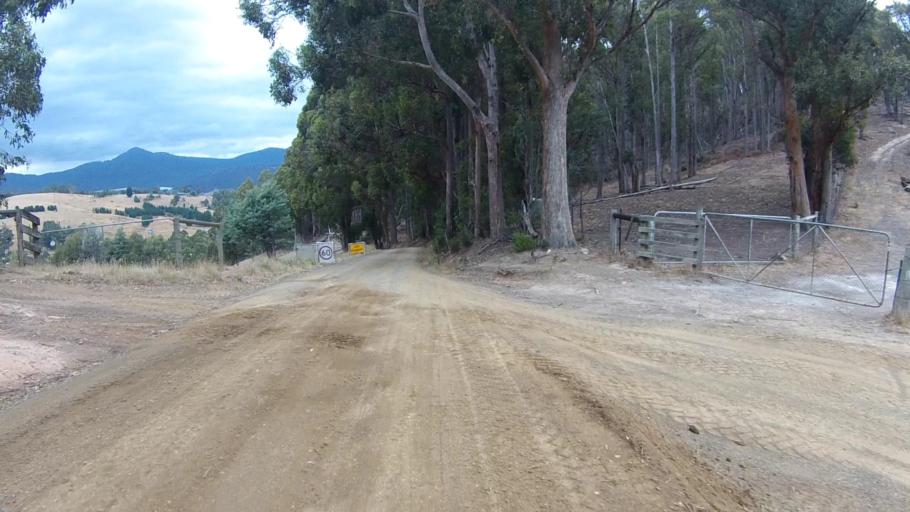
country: AU
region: Tasmania
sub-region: Huon Valley
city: Huonville
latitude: -42.9695
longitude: 147.0471
